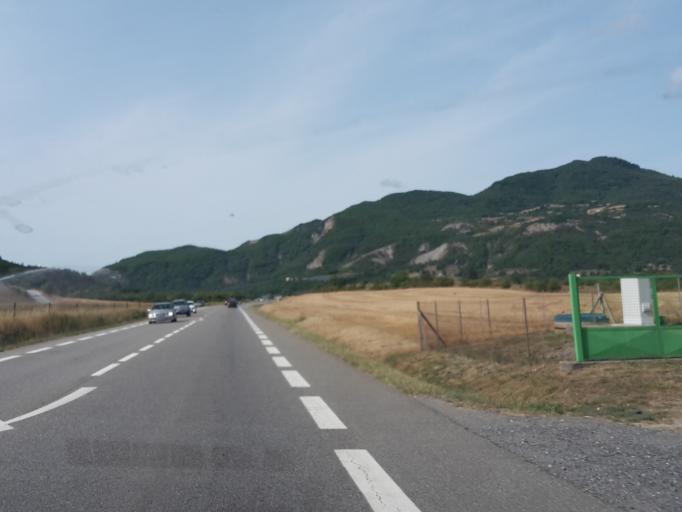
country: FR
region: Provence-Alpes-Cote d'Azur
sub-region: Departement des Hautes-Alpes
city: Tallard
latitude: 44.4536
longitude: 6.0431
